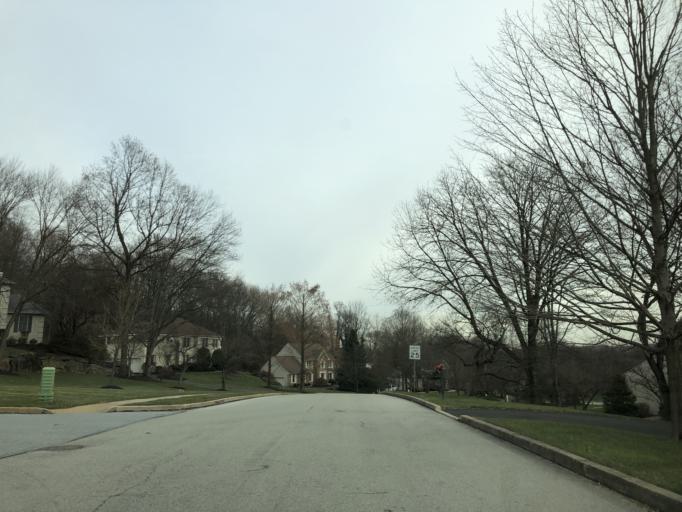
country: US
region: Pennsylvania
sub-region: Chester County
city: Exton
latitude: 40.0380
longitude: -75.6416
